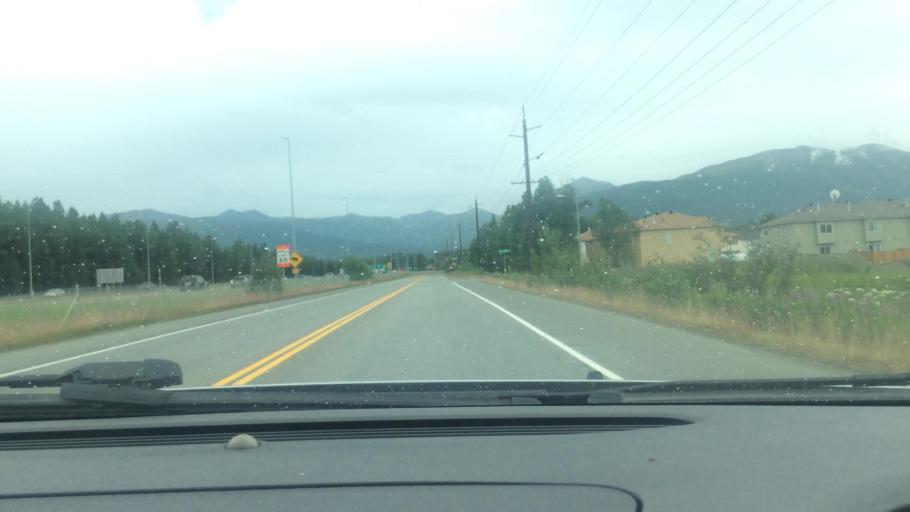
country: US
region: Alaska
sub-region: Anchorage Municipality
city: Anchorage
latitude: 61.2242
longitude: -149.7656
